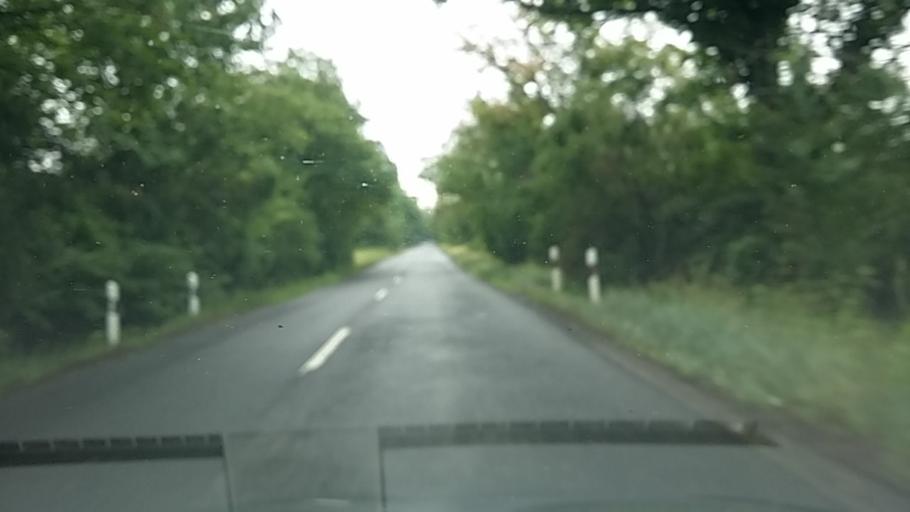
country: HU
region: Pest
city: Szob
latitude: 47.9508
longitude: 18.7812
